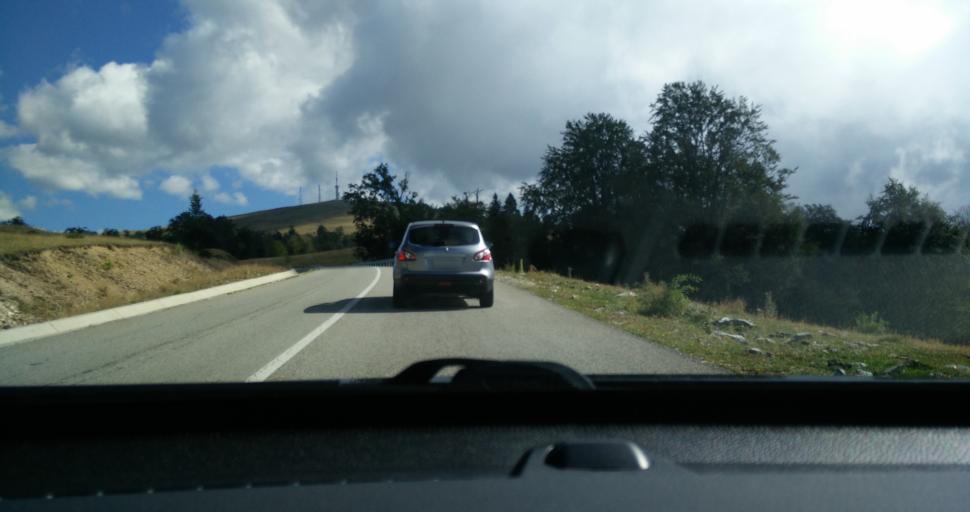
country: RO
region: Gorj
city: Novaci-Straini
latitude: 45.2347
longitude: 23.6903
